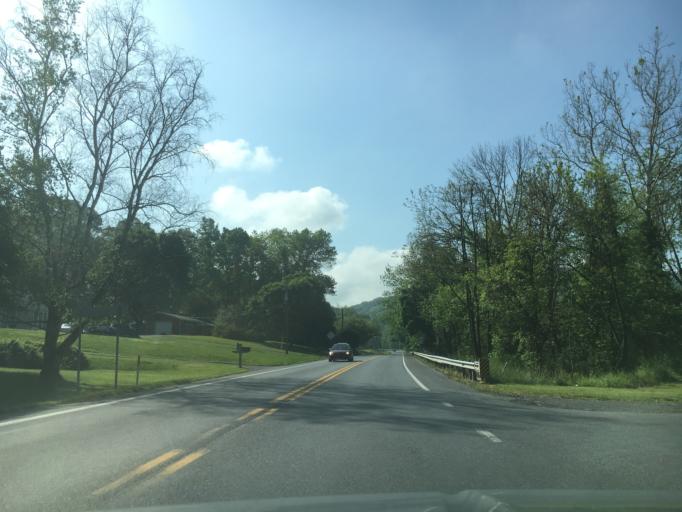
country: US
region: Pennsylvania
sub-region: Berks County
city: Oley
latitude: 40.3785
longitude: -75.7233
